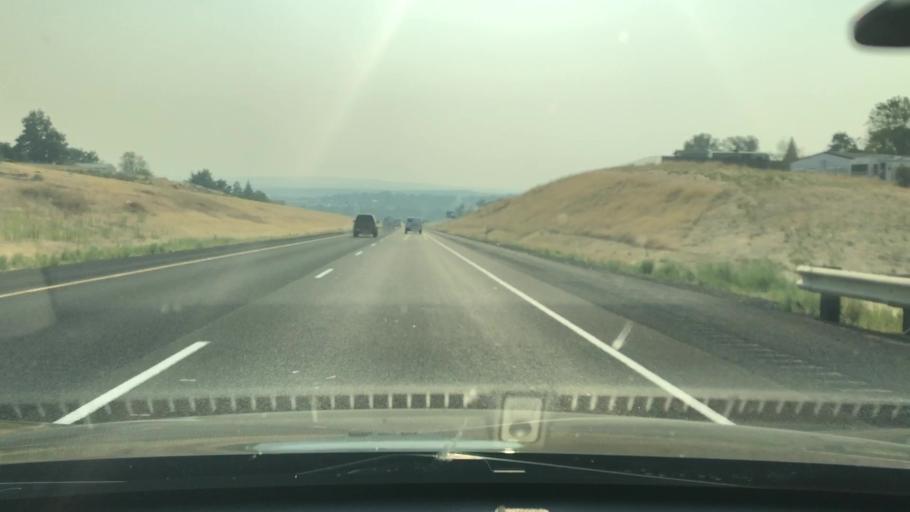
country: US
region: Oregon
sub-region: Umatilla County
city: Pendleton
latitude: 45.6623
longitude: -118.7869
